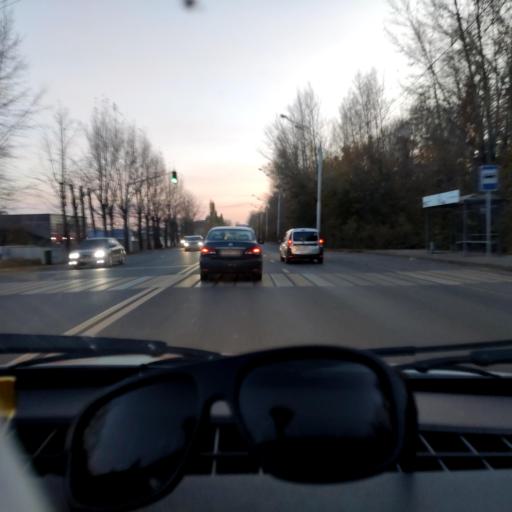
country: RU
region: Bashkortostan
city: Avdon
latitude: 54.6900
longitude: 55.8176
